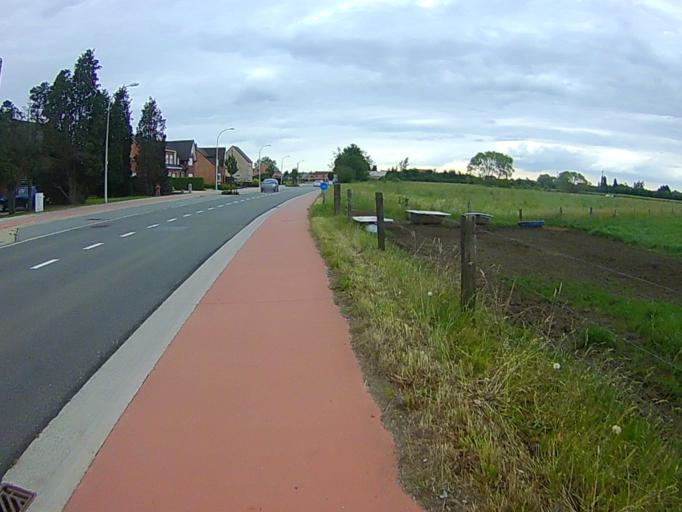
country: BE
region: Flanders
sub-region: Provincie Antwerpen
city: Putte
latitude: 51.0880
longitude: 4.6227
